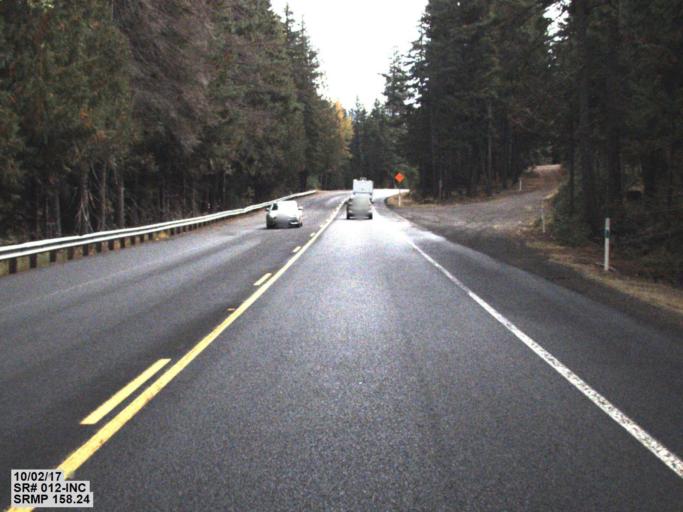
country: US
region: Washington
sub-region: Yakima County
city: Tieton
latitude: 46.6450
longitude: -121.2661
